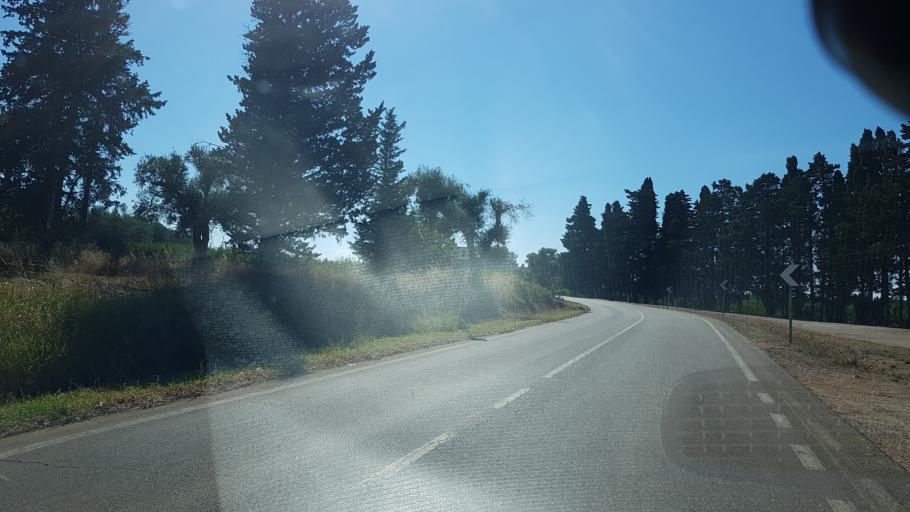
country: IT
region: Apulia
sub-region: Provincia di Brindisi
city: Mesagne
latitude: 40.5575
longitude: 17.8472
